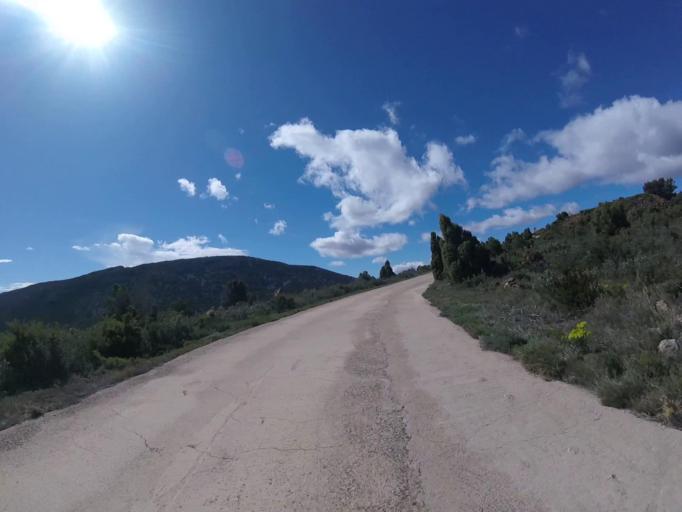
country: ES
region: Valencia
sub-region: Provincia de Castello
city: Culla
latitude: 40.3112
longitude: -0.0972
